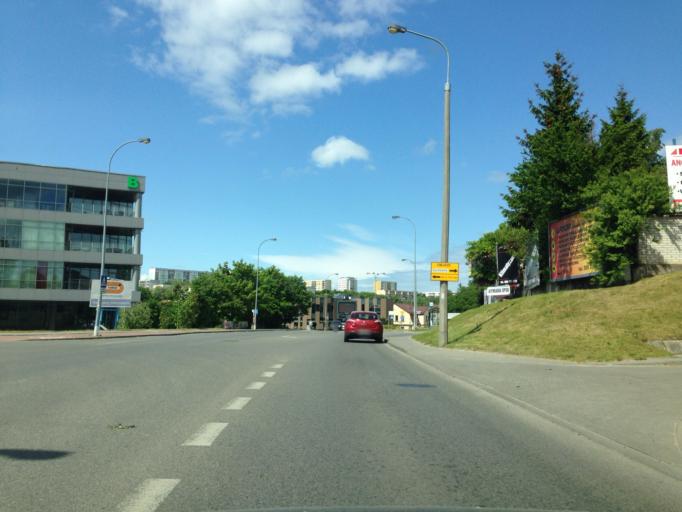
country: PL
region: Pomeranian Voivodeship
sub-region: Gdansk
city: Gdansk
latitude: 54.3538
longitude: 18.5958
